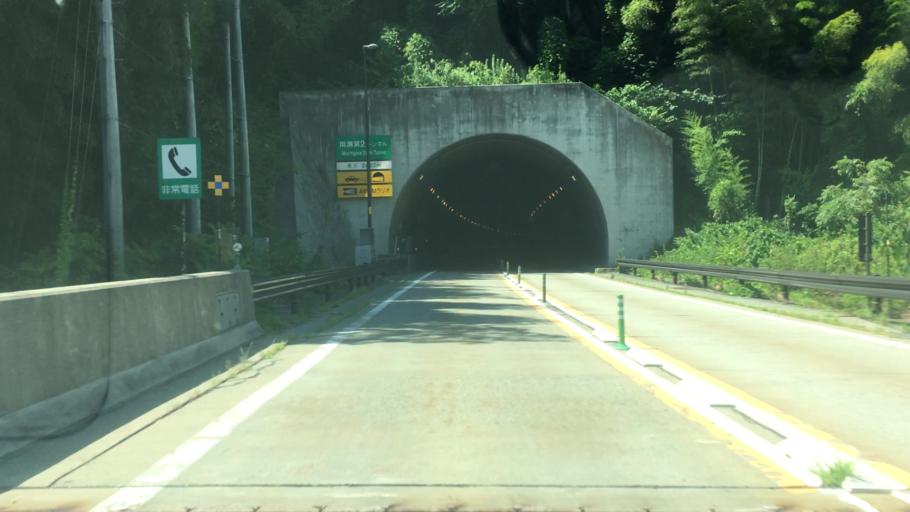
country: JP
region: Tottori
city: Tottori
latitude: 35.3109
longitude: 134.1858
